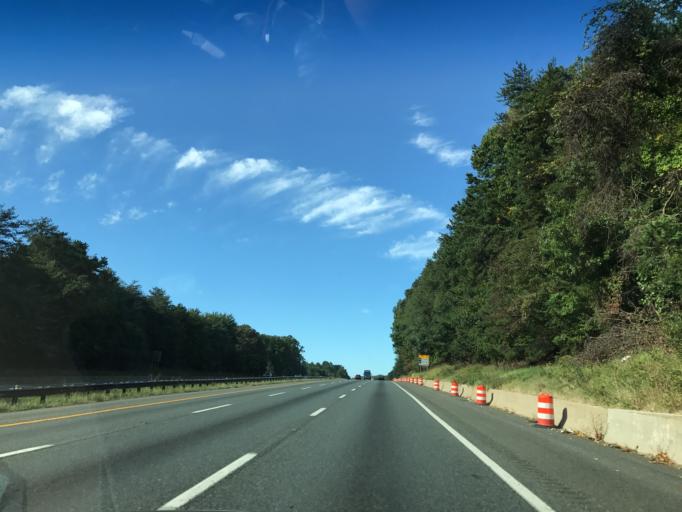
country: US
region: Maryland
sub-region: Anne Arundel County
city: Riva
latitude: 38.9791
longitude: -76.6098
